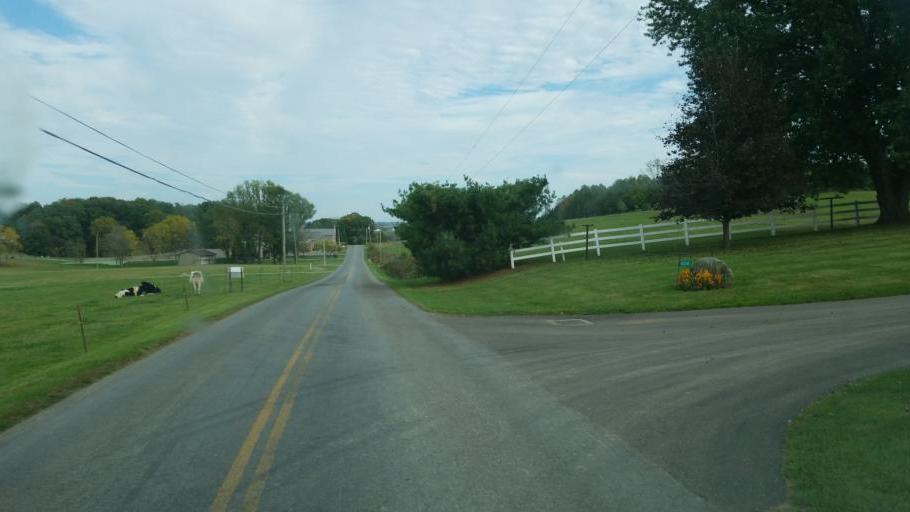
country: US
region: Ohio
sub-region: Holmes County
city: Millersburg
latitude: 40.5730
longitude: -81.8458
